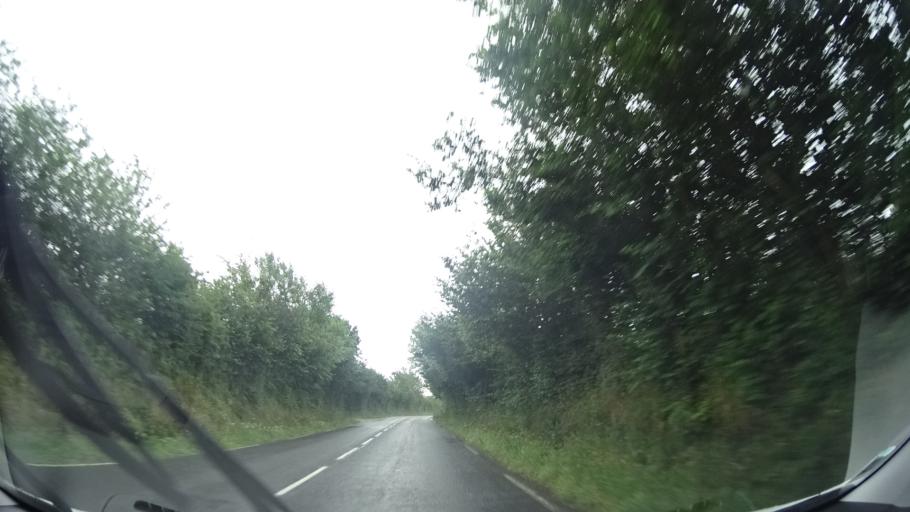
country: FR
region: Lower Normandy
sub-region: Departement de la Manche
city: Beaumont-Hague
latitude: 49.6022
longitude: -1.7818
